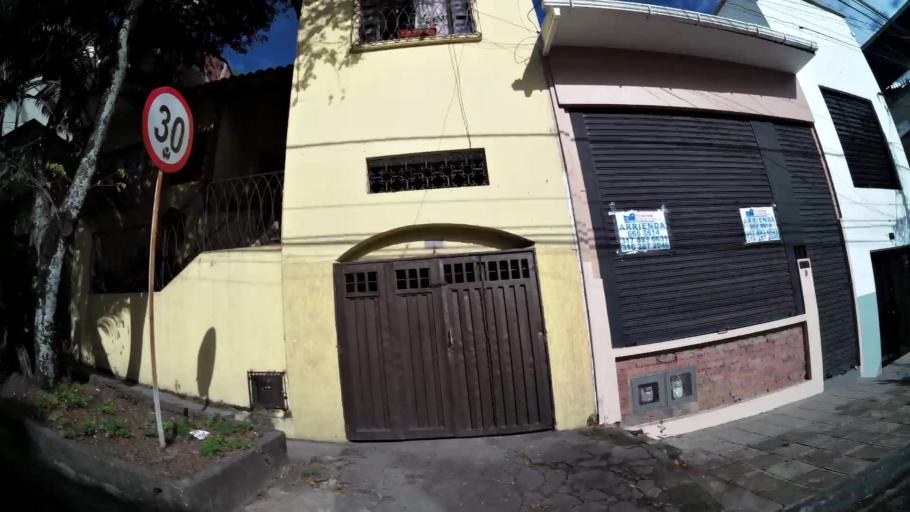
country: CO
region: Valle del Cauca
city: Cali
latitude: 3.4595
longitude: -76.5353
